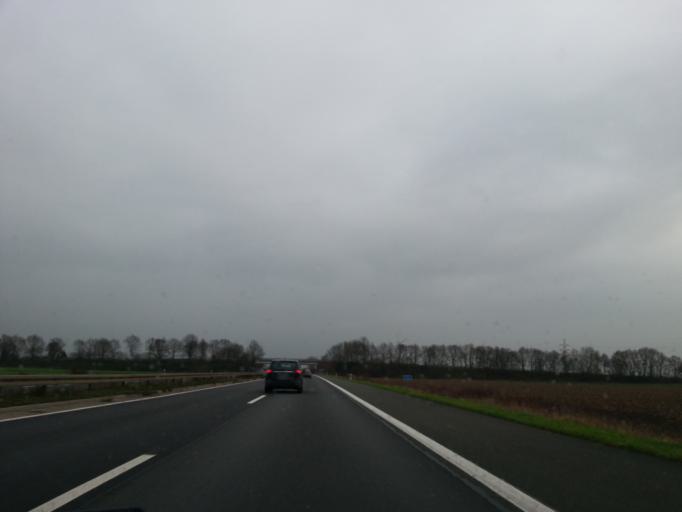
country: NL
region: Gelderland
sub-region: Gemeente Montferland
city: s-Heerenberg
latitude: 51.8517
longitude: 6.2908
